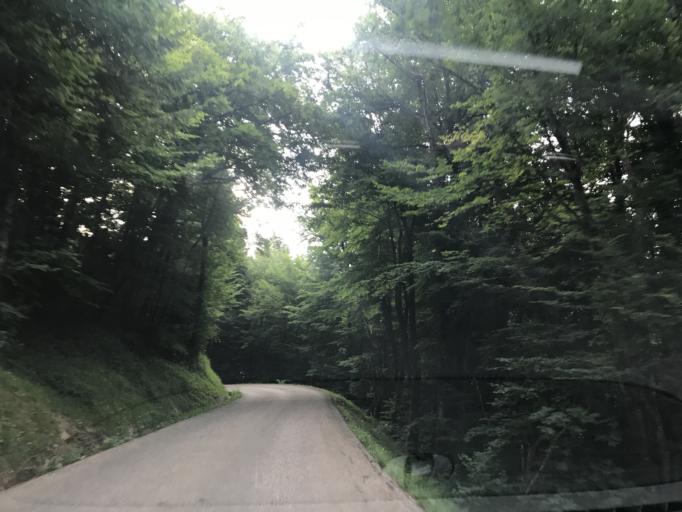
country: FR
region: Rhone-Alpes
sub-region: Departement de l'Isere
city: Saint-Vincent-de-Mercuze
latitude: 45.3950
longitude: 5.9359
